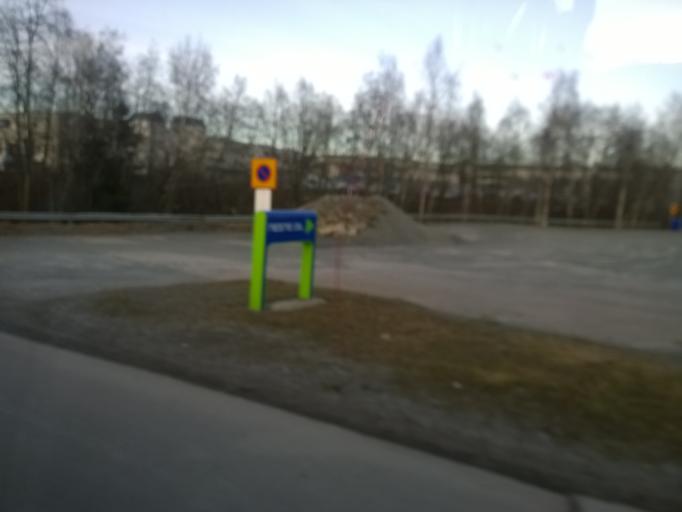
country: FI
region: Pirkanmaa
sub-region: Tampere
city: Tampere
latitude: 61.4774
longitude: 23.7639
